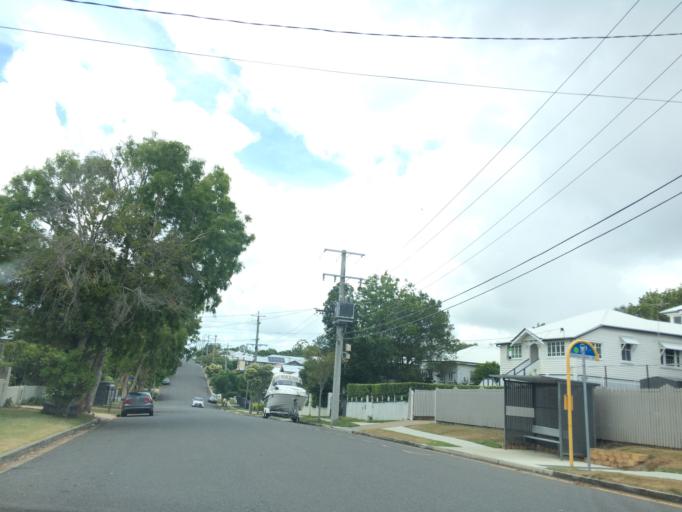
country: AU
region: Queensland
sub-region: Brisbane
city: Balmoral
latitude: -27.4466
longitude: 153.0565
